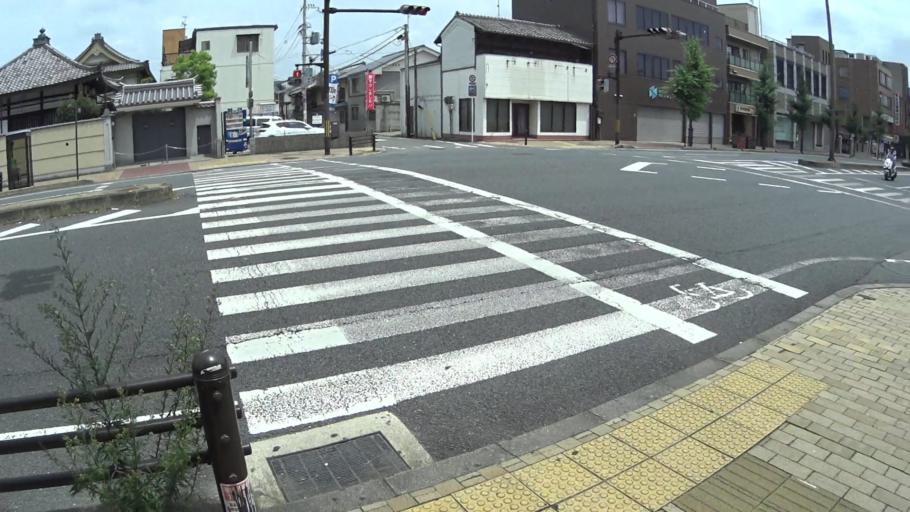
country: JP
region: Kyoto
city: Kyoto
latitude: 34.9791
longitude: 135.7506
